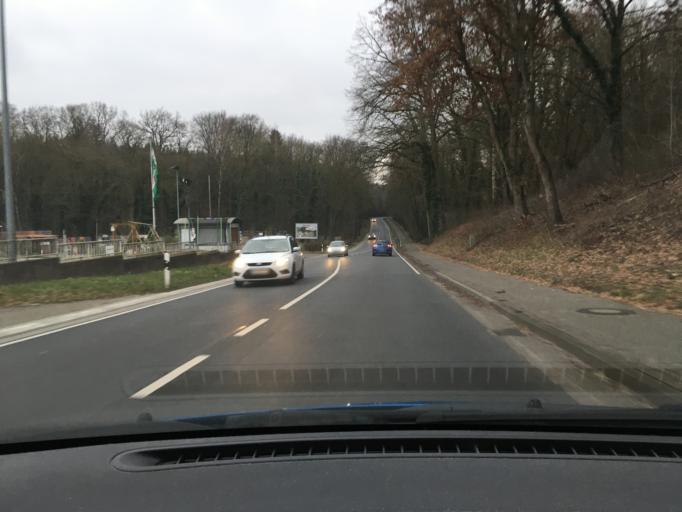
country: DE
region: Lower Saxony
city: Walsrode
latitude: 52.8586
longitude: 9.6059
